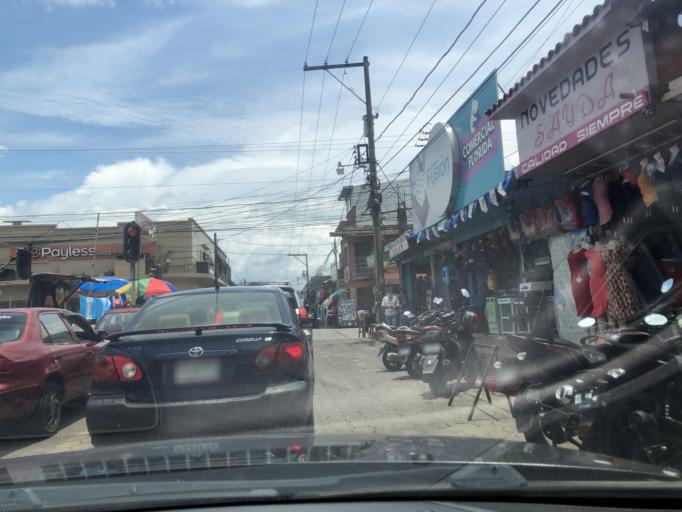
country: GT
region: Quetzaltenango
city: Coatepeque
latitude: 14.7045
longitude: -91.8635
